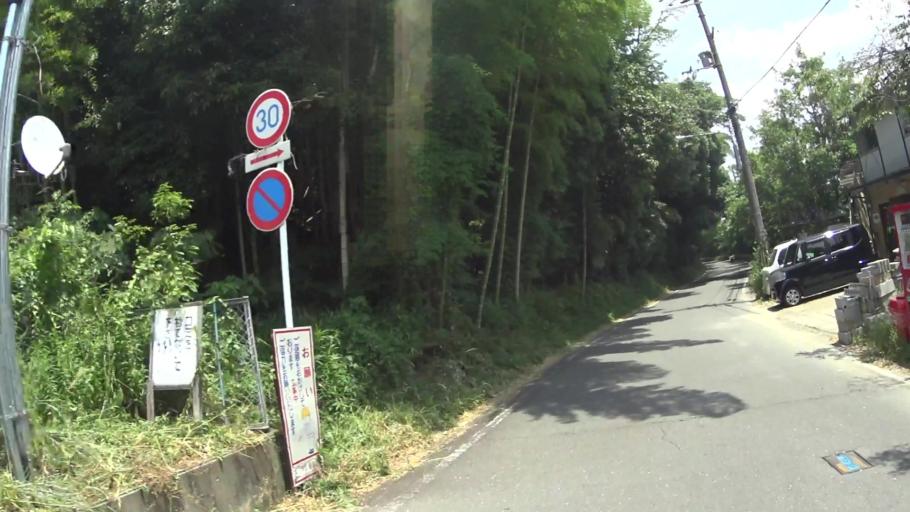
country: JP
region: Kyoto
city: Muko
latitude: 34.9722
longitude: 135.6849
